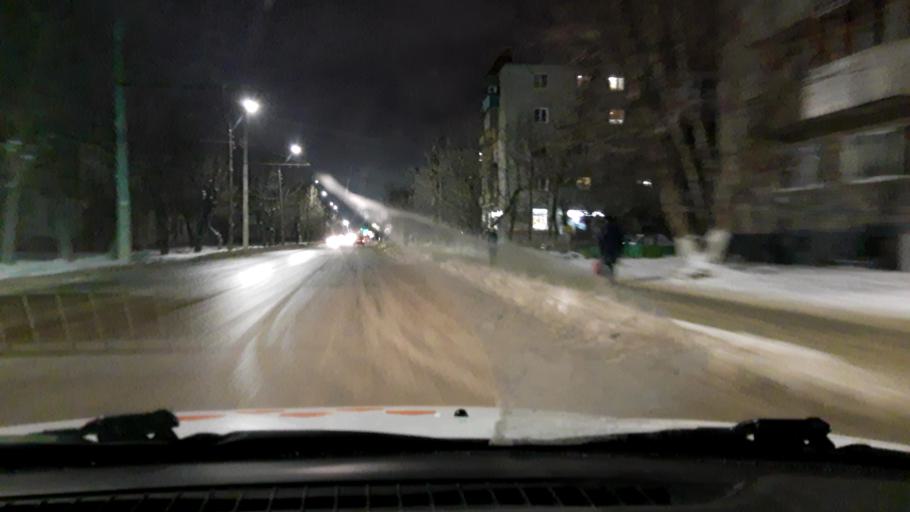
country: RU
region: Nizjnij Novgorod
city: Dzerzhinsk
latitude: 56.2352
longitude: 43.4804
